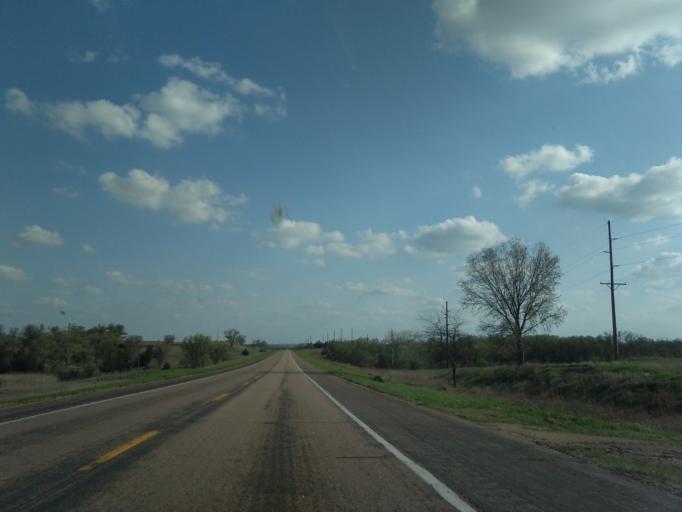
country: US
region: Nebraska
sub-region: Webster County
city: Red Cloud
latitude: 40.1168
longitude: -98.5189
